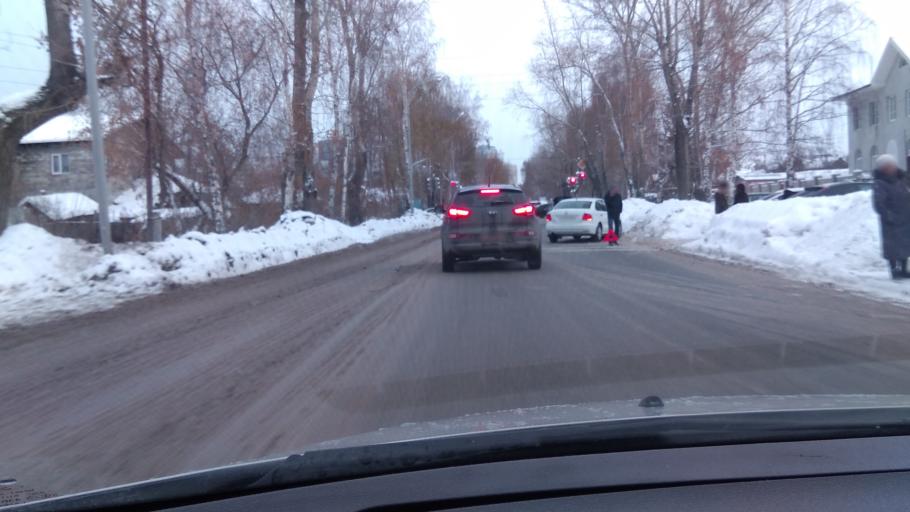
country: RU
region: Sverdlovsk
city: Yekaterinburg
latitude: 56.8091
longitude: 60.5850
